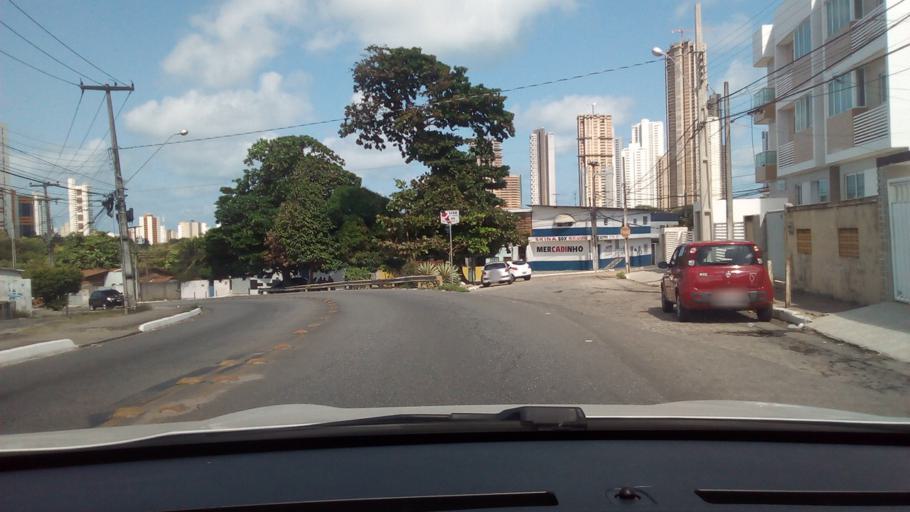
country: BR
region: Paraiba
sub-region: Joao Pessoa
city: Joao Pessoa
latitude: -7.1292
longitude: -34.8376
